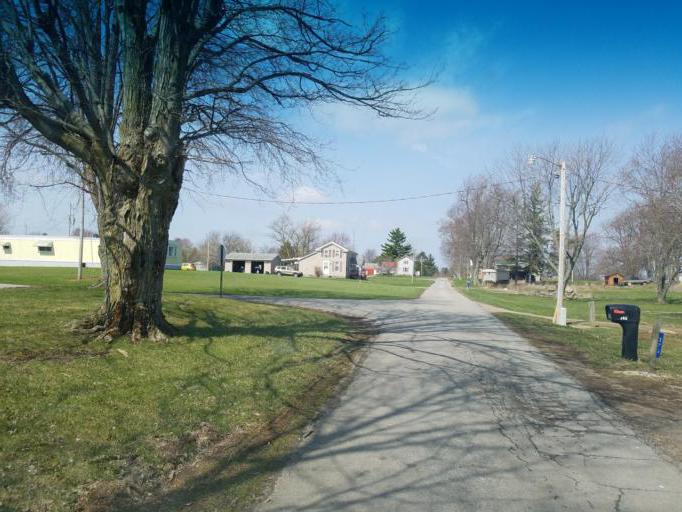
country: US
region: Ohio
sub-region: Crawford County
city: Bucyrus
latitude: 40.9284
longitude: -83.0944
